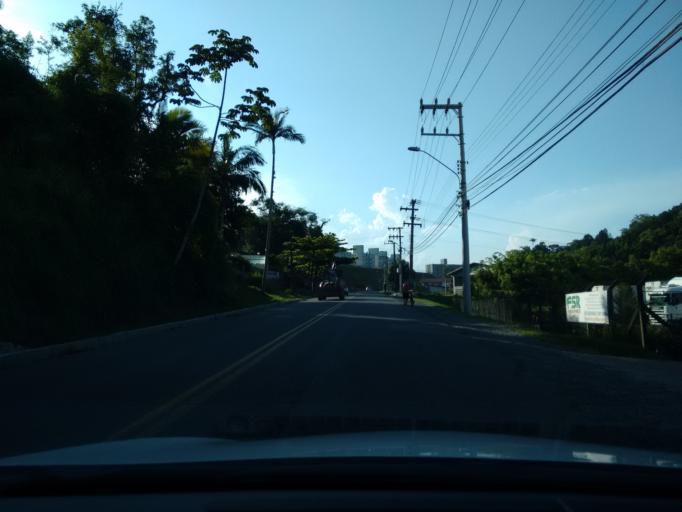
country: BR
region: Santa Catarina
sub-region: Blumenau
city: Blumenau
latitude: -26.8599
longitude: -49.1030
